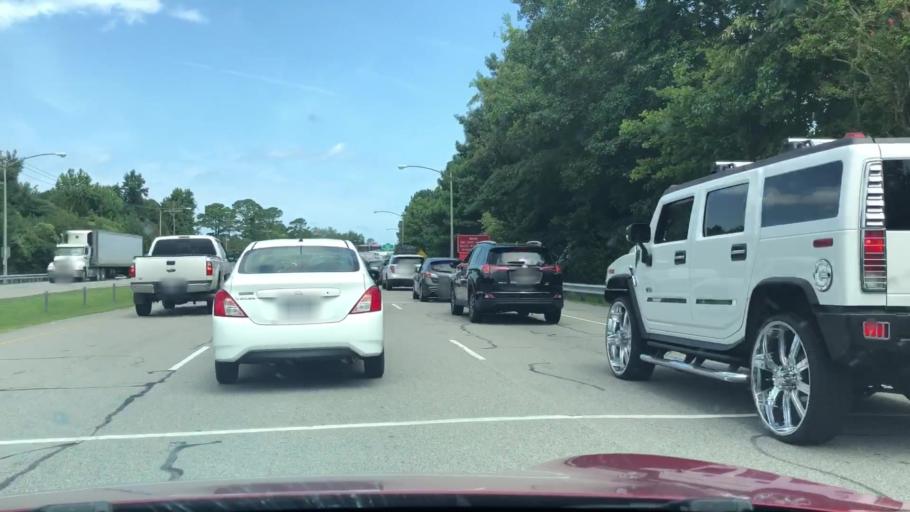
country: US
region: Virginia
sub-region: City of Virginia Beach
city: Virginia Beach
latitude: 36.9092
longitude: -76.1303
